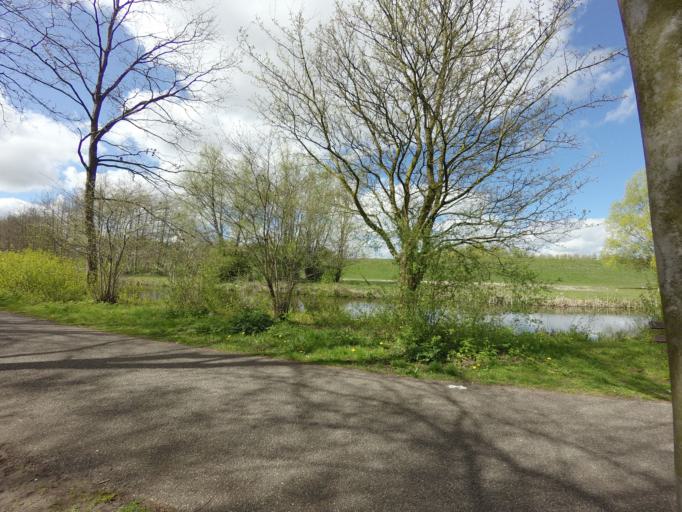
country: NL
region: South Holland
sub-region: Gemeente Gouda
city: Bloemendaal
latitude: 52.0273
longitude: 4.6852
